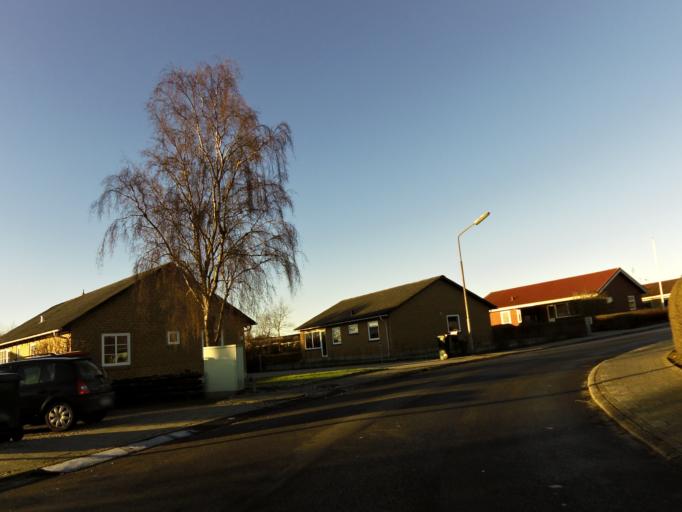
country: DK
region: South Denmark
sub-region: Tonder Kommune
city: Sherrebek
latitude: 55.1516
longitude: 8.7718
